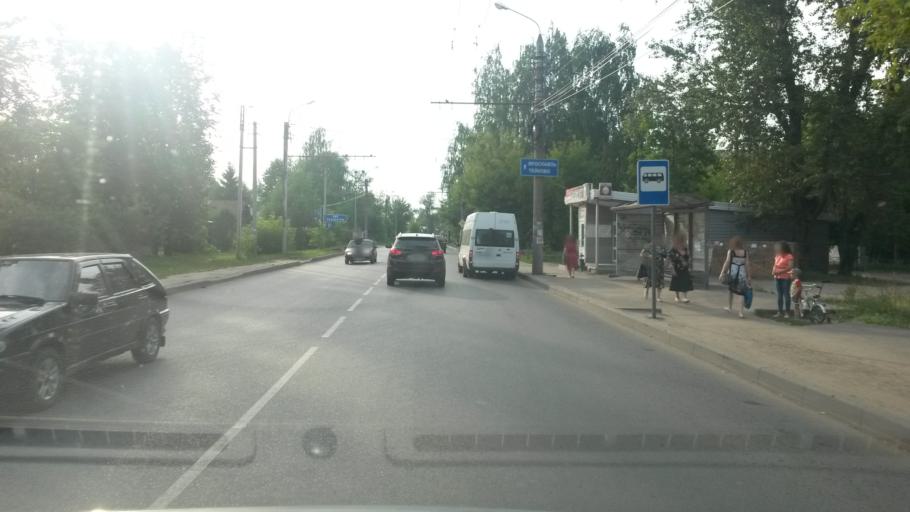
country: RU
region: Ivanovo
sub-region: Gorod Ivanovo
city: Ivanovo
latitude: 57.0096
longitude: 40.9429
